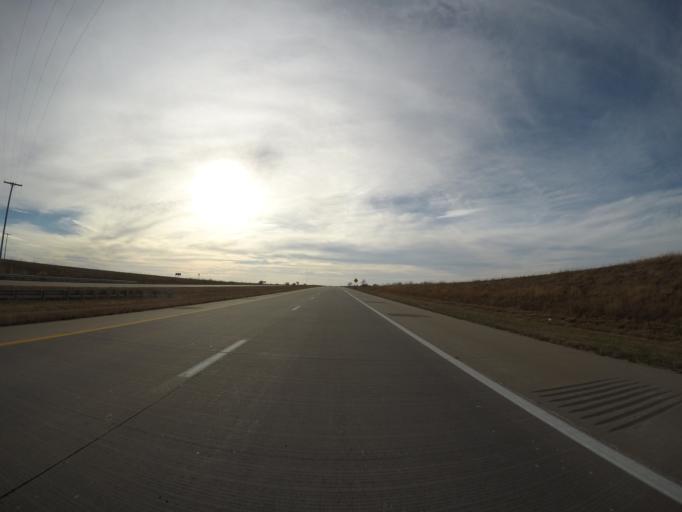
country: US
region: Kansas
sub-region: Franklin County
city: Wellsville
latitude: 38.6703
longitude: -95.1561
